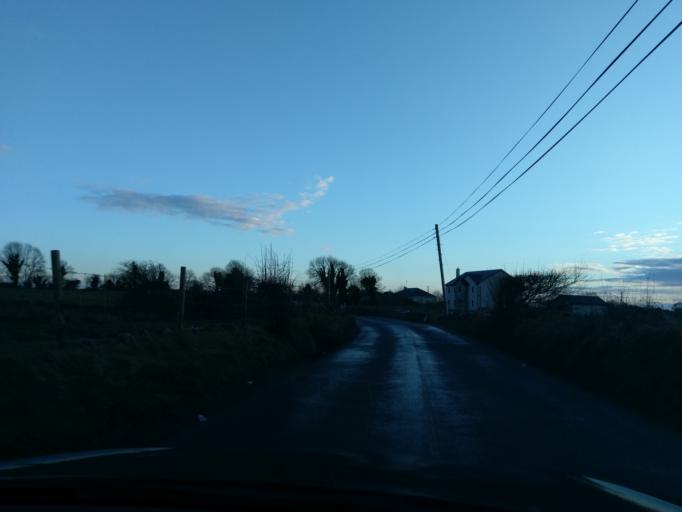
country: IE
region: Connaught
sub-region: County Galway
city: Athenry
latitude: 53.2884
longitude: -8.6350
